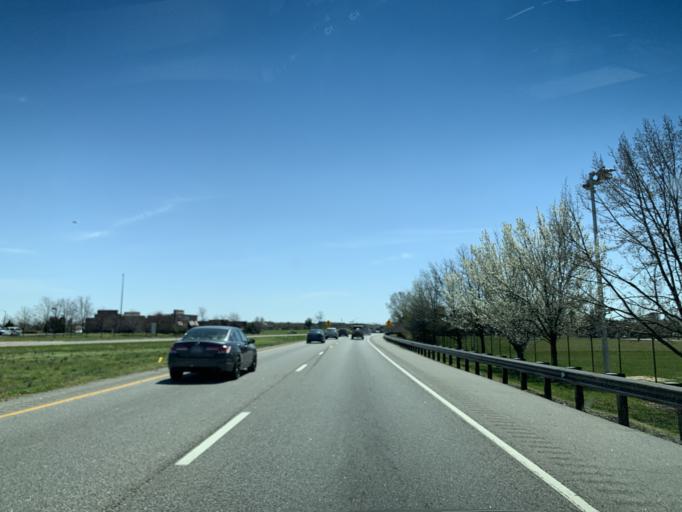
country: US
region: Maryland
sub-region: Talbot County
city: Easton
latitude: 38.7962
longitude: -76.0606
